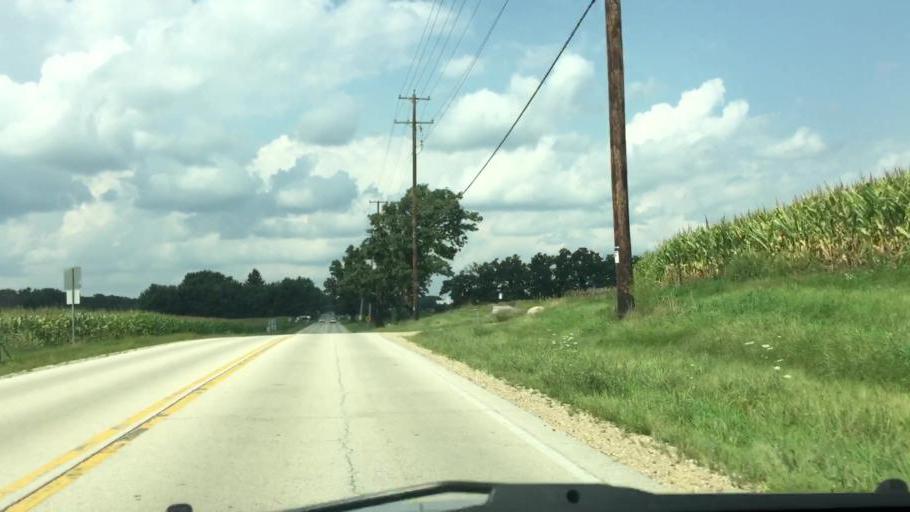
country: US
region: Wisconsin
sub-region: Waukesha County
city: North Prairie
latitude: 42.9415
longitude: -88.4055
